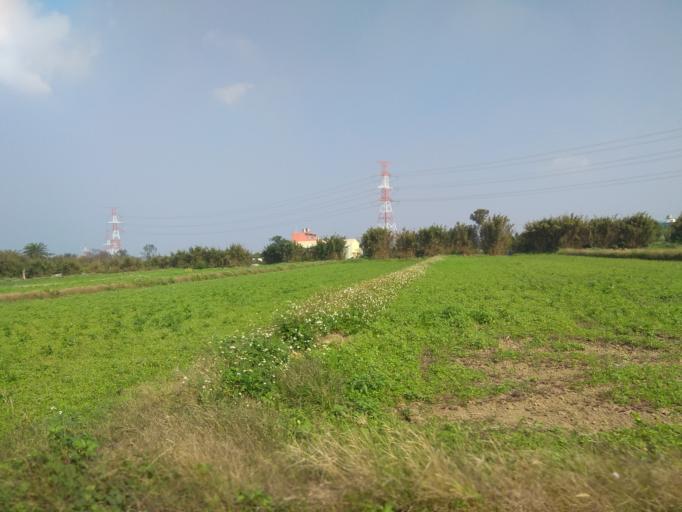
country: TW
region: Taiwan
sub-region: Hsinchu
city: Zhubei
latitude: 24.9996
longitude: 121.0574
